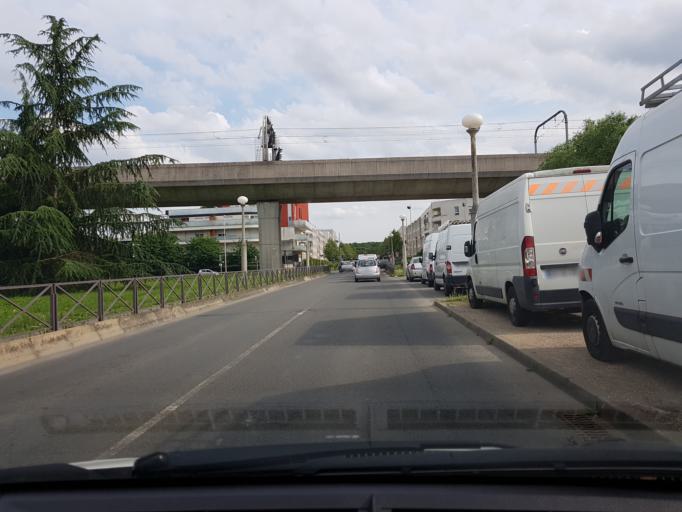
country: FR
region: Ile-de-France
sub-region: Departement de Seine-et-Marne
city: Torcy
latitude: 48.8395
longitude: 2.6489
